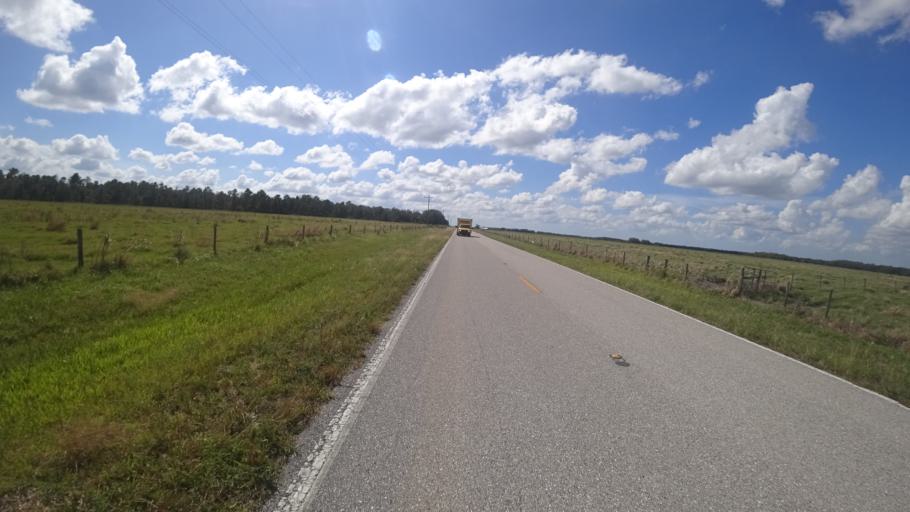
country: US
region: Florida
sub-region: Sarasota County
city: Lake Sarasota
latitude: 27.3183
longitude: -82.1737
